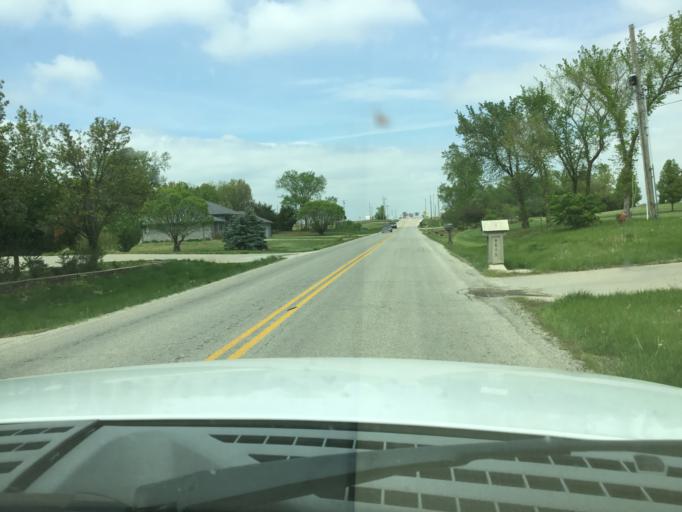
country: US
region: Kansas
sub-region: Shawnee County
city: Topeka
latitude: 38.9828
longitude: -95.6144
